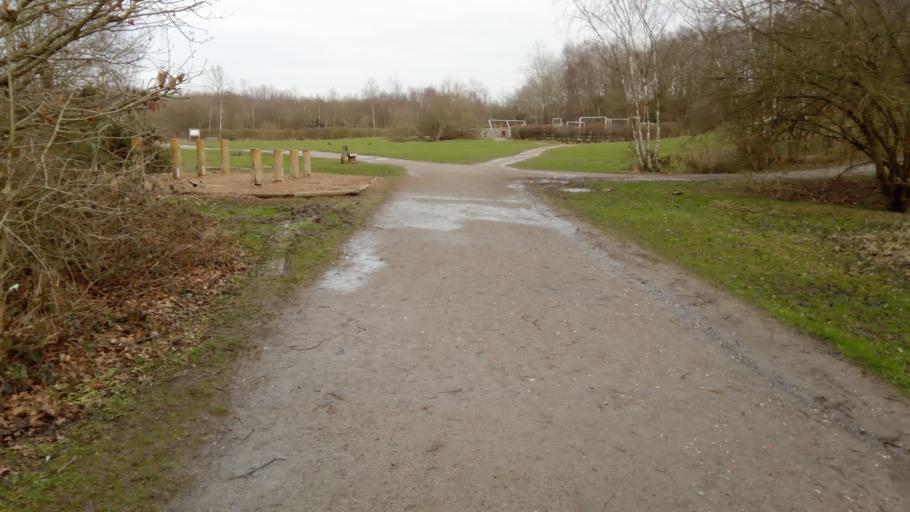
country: GB
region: England
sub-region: Medway
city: Cuxton
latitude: 51.4049
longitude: 0.4204
